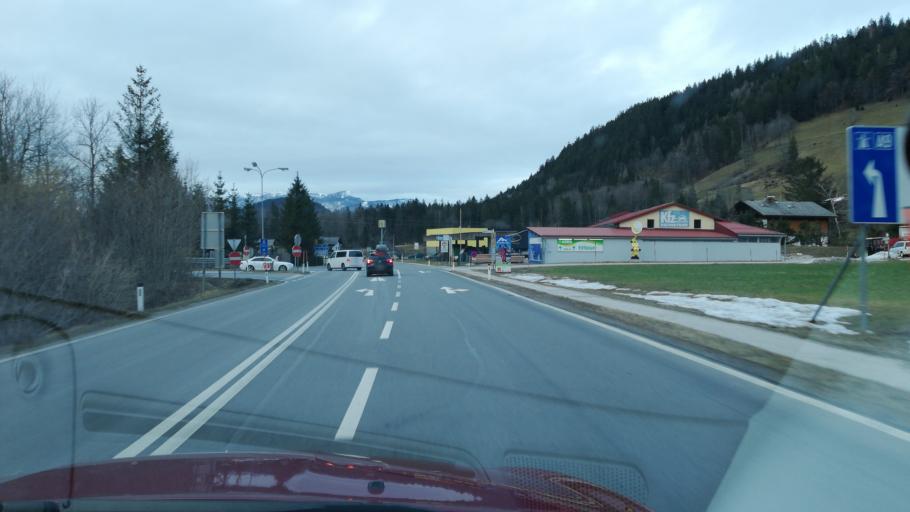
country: AT
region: Styria
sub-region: Politischer Bezirk Liezen
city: Ardning
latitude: 47.6488
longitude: 14.3367
